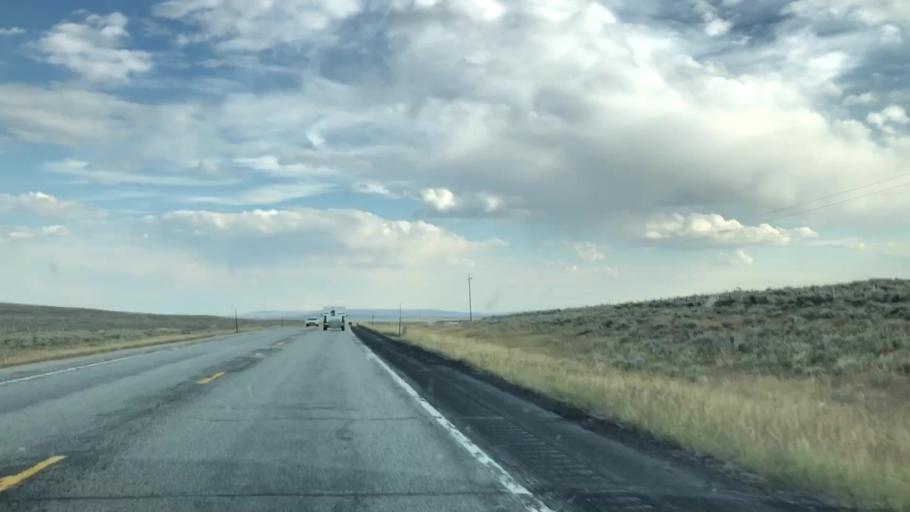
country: US
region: Wyoming
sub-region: Sublette County
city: Pinedale
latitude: 43.0561
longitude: -110.1557
